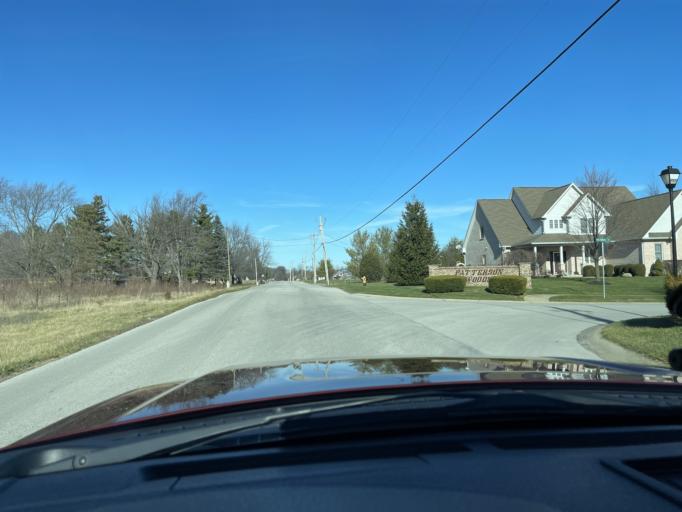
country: US
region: Indiana
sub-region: Hendricks County
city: Avon
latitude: 39.7584
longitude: -86.4572
